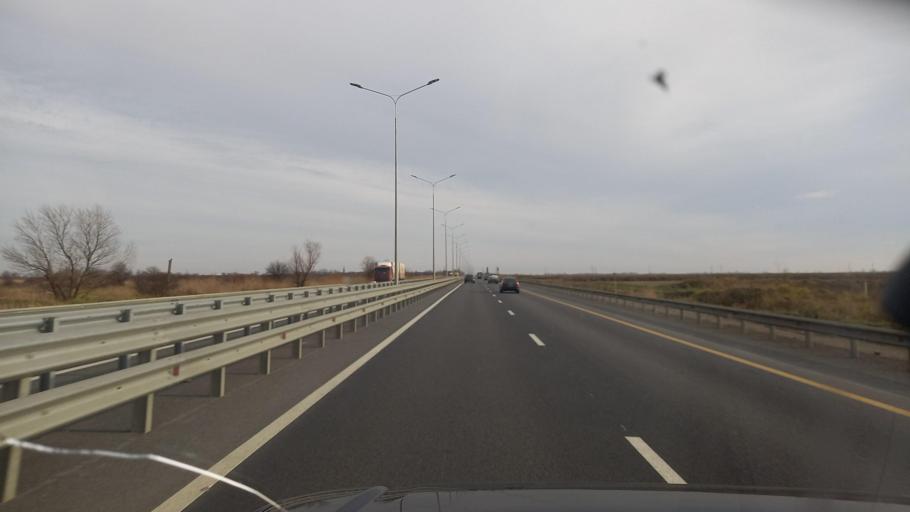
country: RU
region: Adygeya
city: Takhtamukay
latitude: 44.9514
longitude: 39.0035
